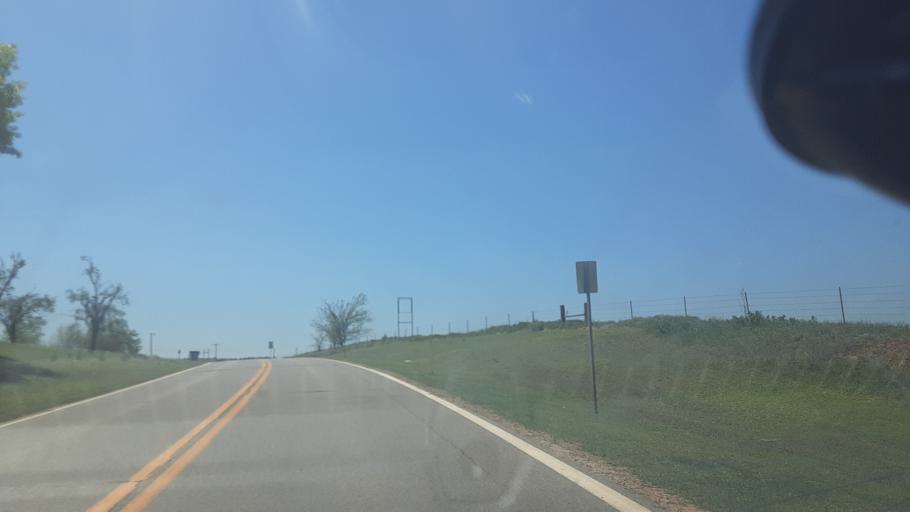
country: US
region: Oklahoma
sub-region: Logan County
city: Guthrie
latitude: 36.0608
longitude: -97.4075
